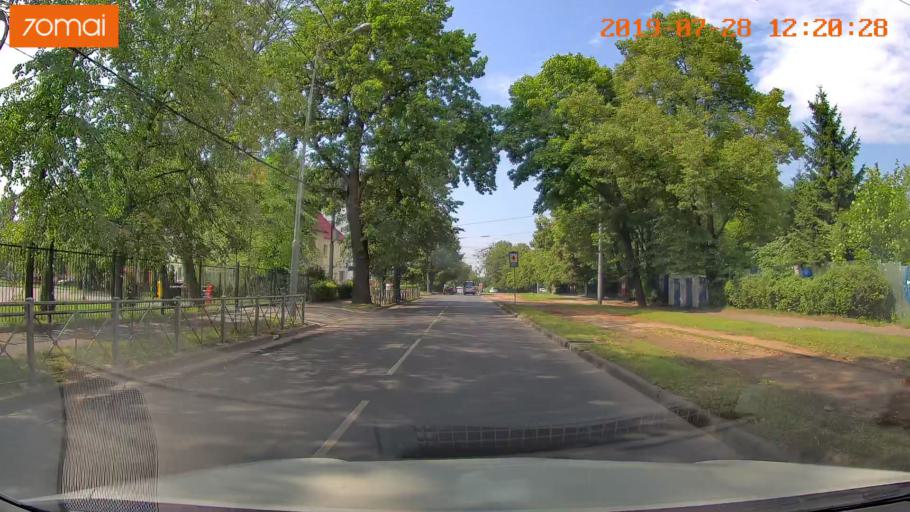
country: RU
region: Kaliningrad
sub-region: Gorod Kaliningrad
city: Kaliningrad
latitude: 54.7139
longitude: 20.4544
